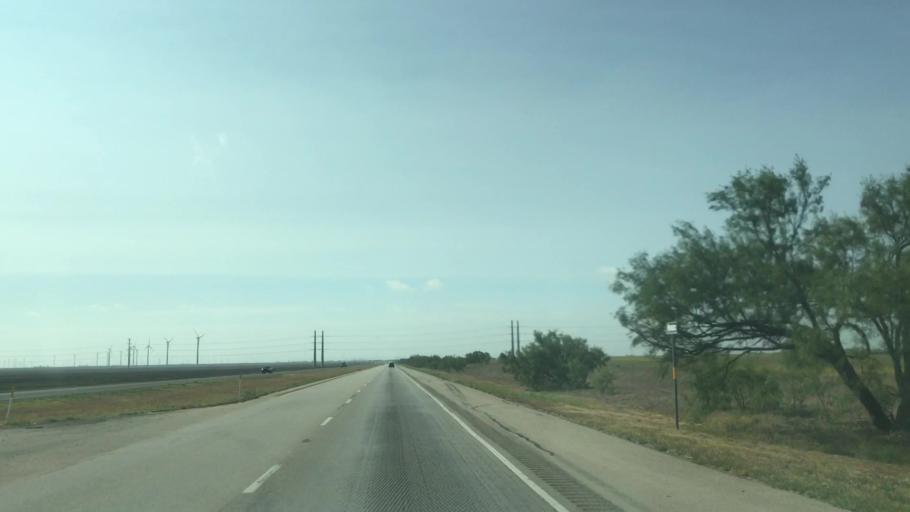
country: US
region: Texas
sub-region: Scurry County
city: Snyder
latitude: 32.6013
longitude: -100.7401
